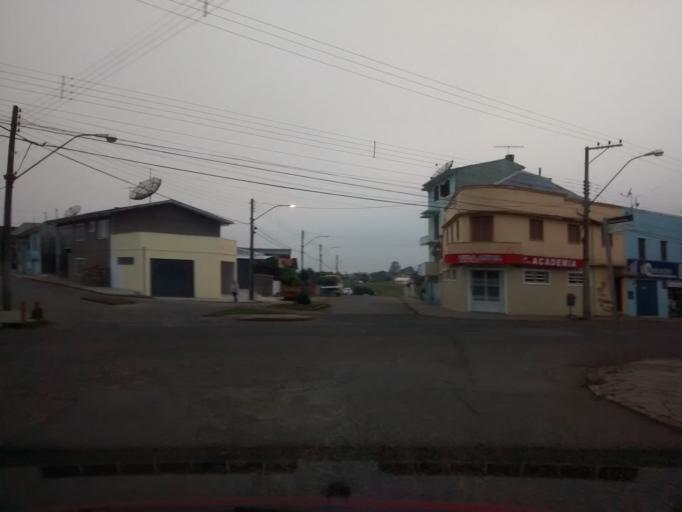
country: BR
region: Rio Grande do Sul
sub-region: Vacaria
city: Vacaria
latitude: -28.5028
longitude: -50.9325
